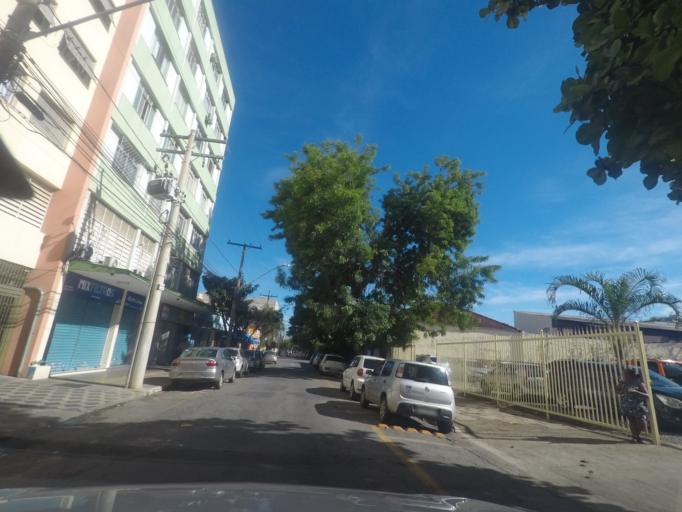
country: BR
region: Goias
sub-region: Goiania
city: Goiania
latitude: -16.6677
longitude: -49.2616
